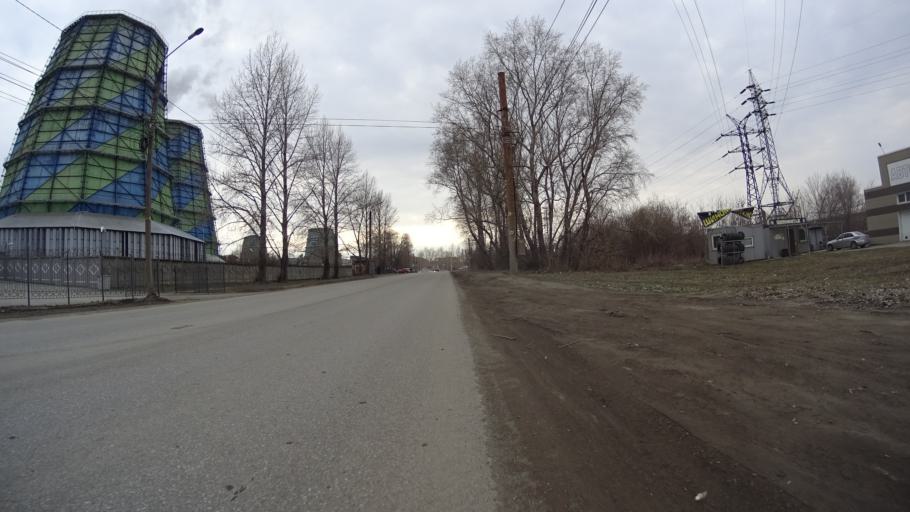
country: RU
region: Chelyabinsk
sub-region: Gorod Chelyabinsk
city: Chelyabinsk
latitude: 55.1563
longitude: 61.5011
